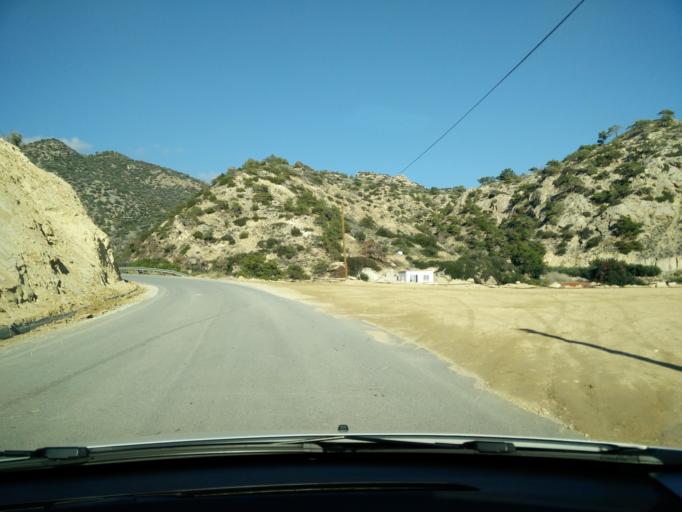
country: GR
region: Crete
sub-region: Nomos Lasithiou
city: Gra Liyia
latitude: 34.9948
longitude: 25.5326
